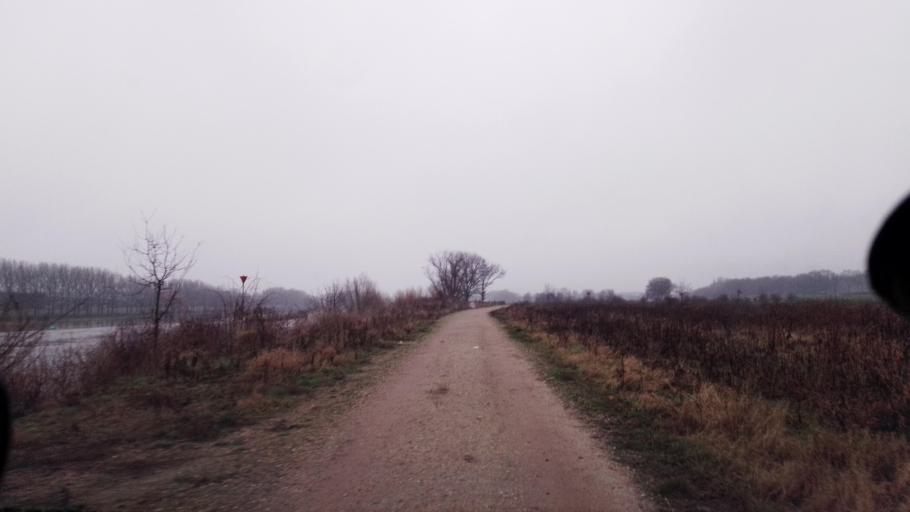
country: NL
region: Limburg
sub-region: Gemeente Venlo
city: Venlo
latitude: 51.3835
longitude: 6.1633
